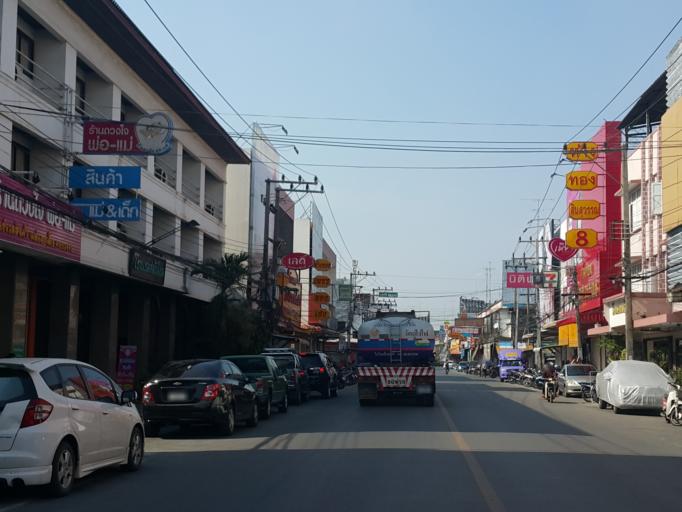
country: TH
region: Phitsanulok
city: Phitsanulok
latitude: 16.8131
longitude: 100.2645
